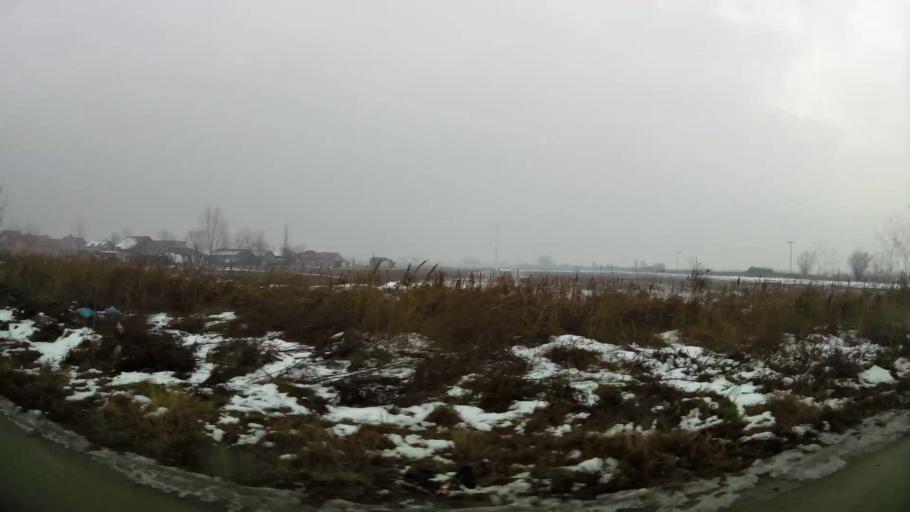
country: MK
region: Petrovec
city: Petrovec
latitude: 41.9338
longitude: 21.6079
